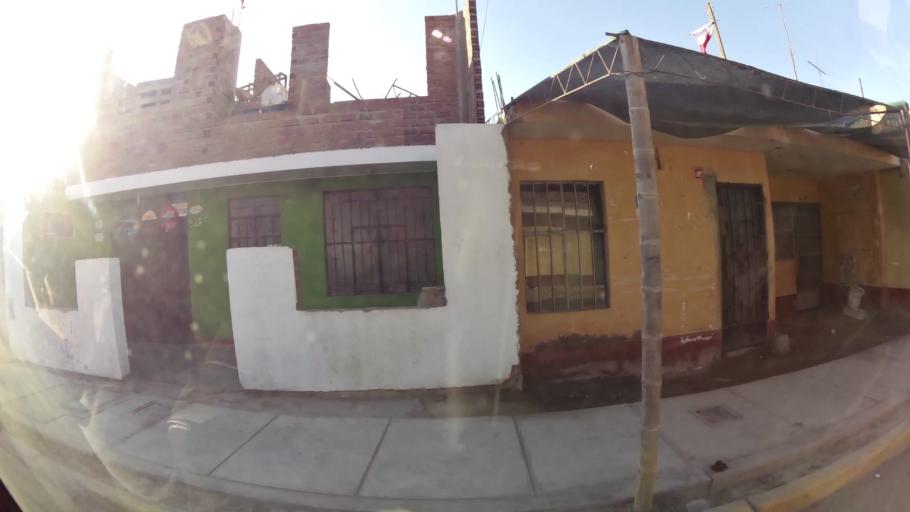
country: PE
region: Ica
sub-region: Provincia de Ica
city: Ica
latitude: -14.0645
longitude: -75.7188
